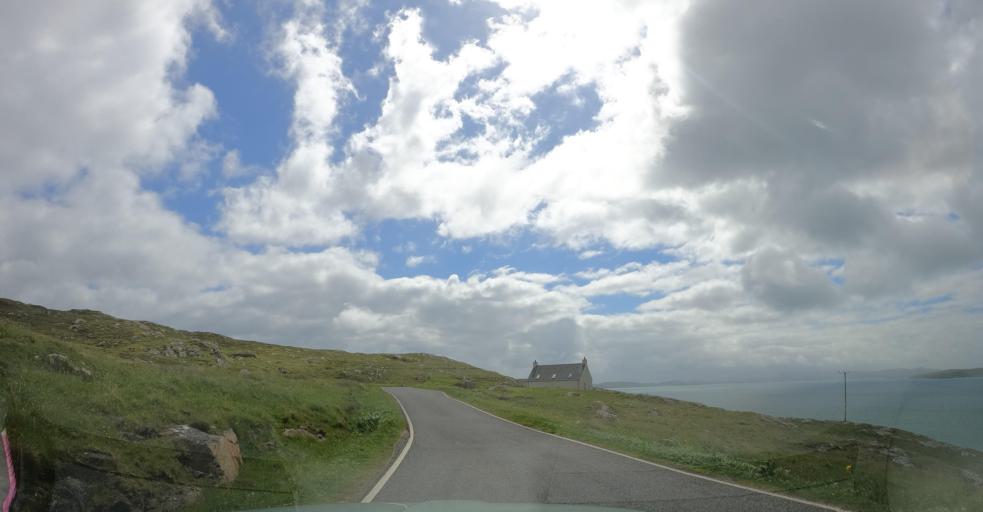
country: GB
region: Scotland
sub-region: Eilean Siar
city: Isle of South Uist
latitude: 57.0780
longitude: -7.3026
